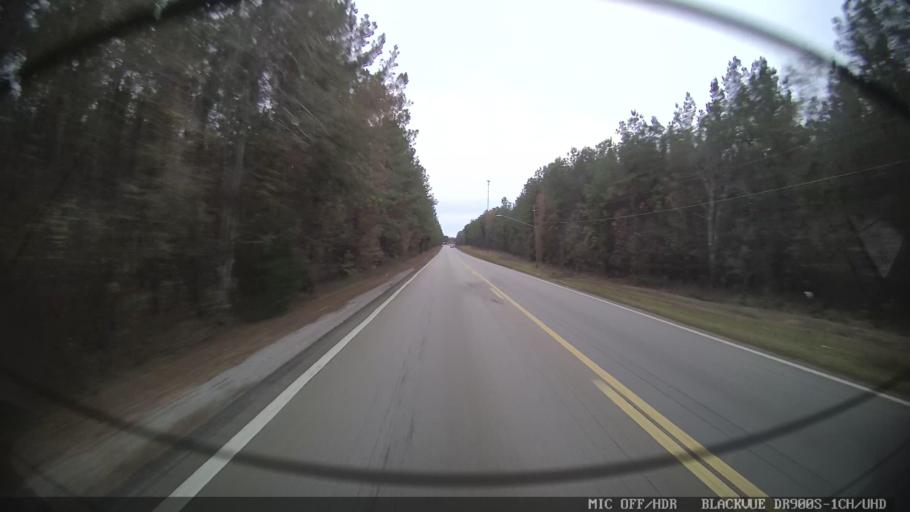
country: US
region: Mississippi
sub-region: Clarke County
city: Stonewall
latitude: 32.0508
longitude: -88.8959
